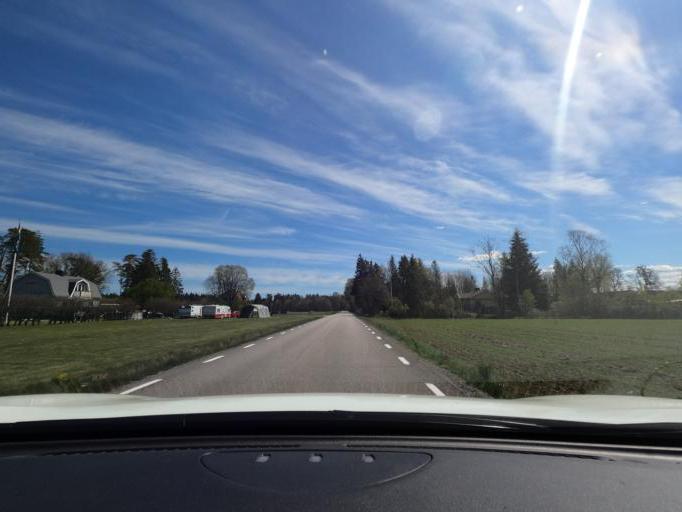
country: SE
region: Vaestra Goetaland
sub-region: Marks Kommun
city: Horred
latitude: 57.4244
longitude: 12.3550
